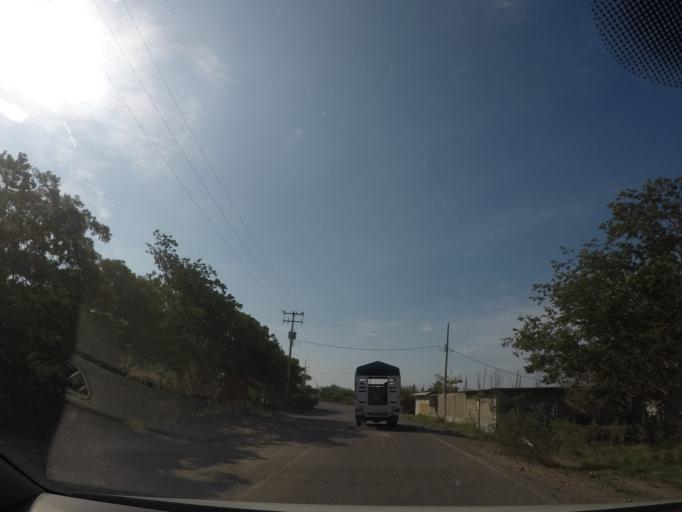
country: MX
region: Oaxaca
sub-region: Salina Cruz
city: Salina Cruz
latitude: 16.2332
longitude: -95.1500
